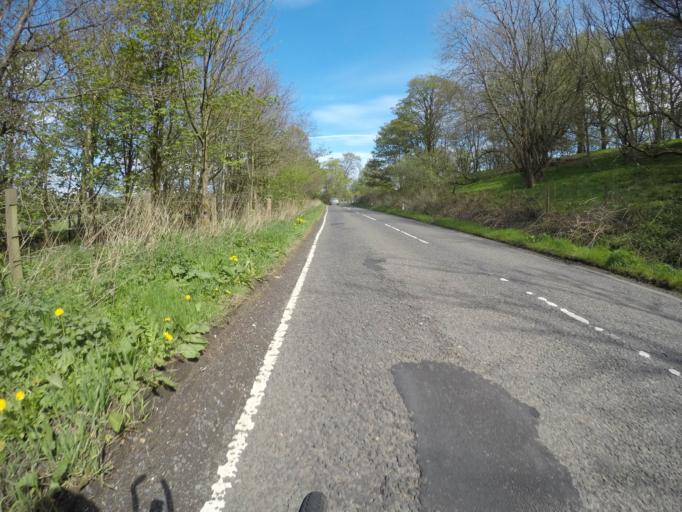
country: GB
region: Scotland
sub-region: East Ayrshire
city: Stewarton
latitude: 55.6741
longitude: -4.5235
